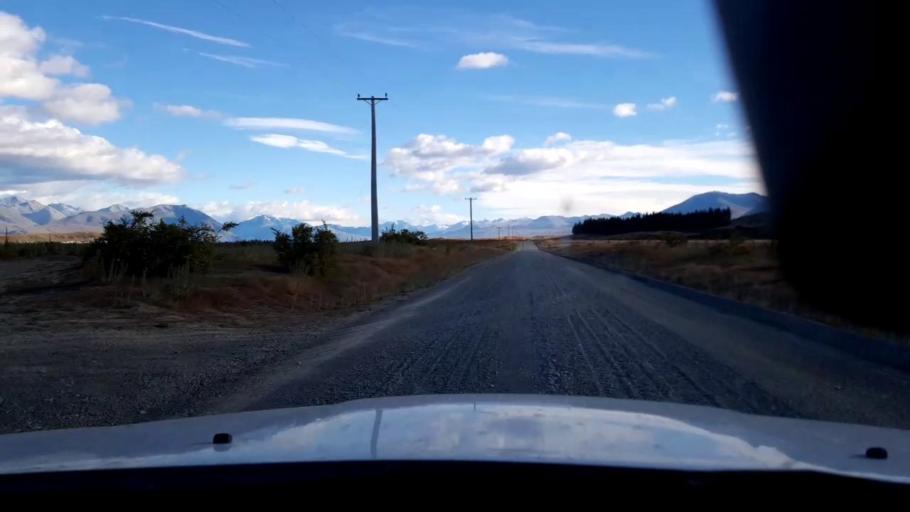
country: NZ
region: Canterbury
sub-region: Timaru District
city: Pleasant Point
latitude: -43.9907
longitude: 170.5024
